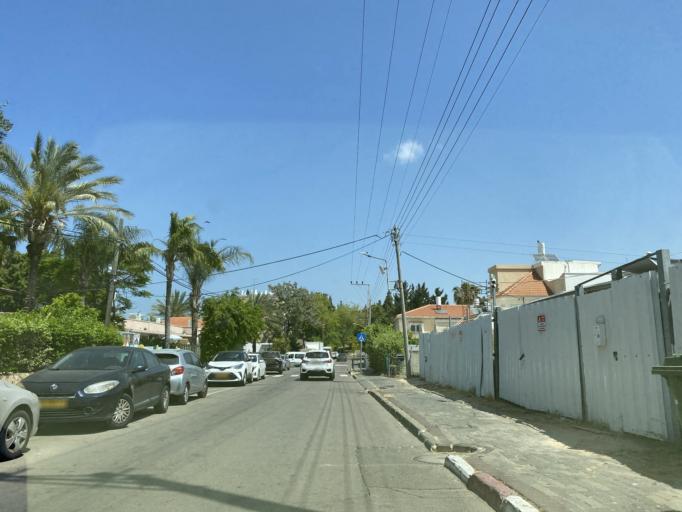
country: IL
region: Tel Aviv
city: Ramat HaSharon
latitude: 32.1552
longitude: 34.8365
